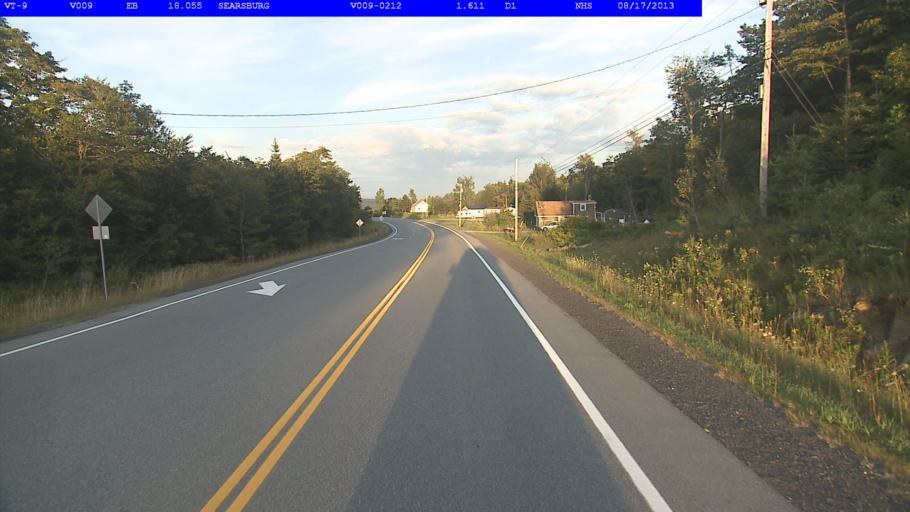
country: US
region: Vermont
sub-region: Windham County
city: Dover
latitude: 42.8951
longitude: -72.9807
